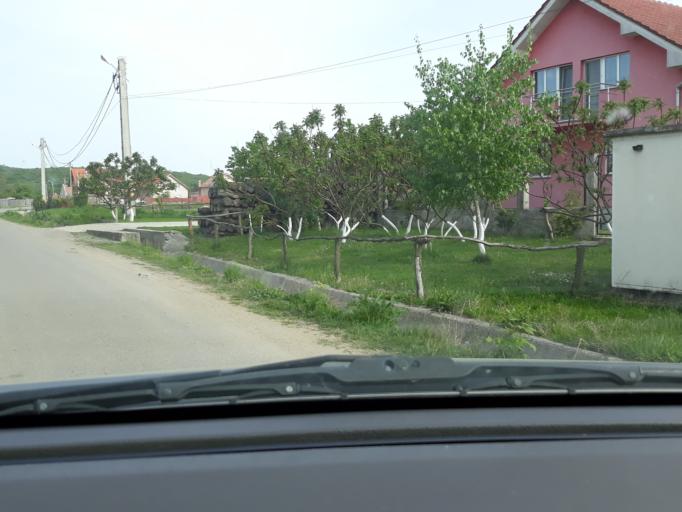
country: RO
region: Bihor
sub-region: Comuna Sanmartin
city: Sanmartin
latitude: 46.9889
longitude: 21.9949
